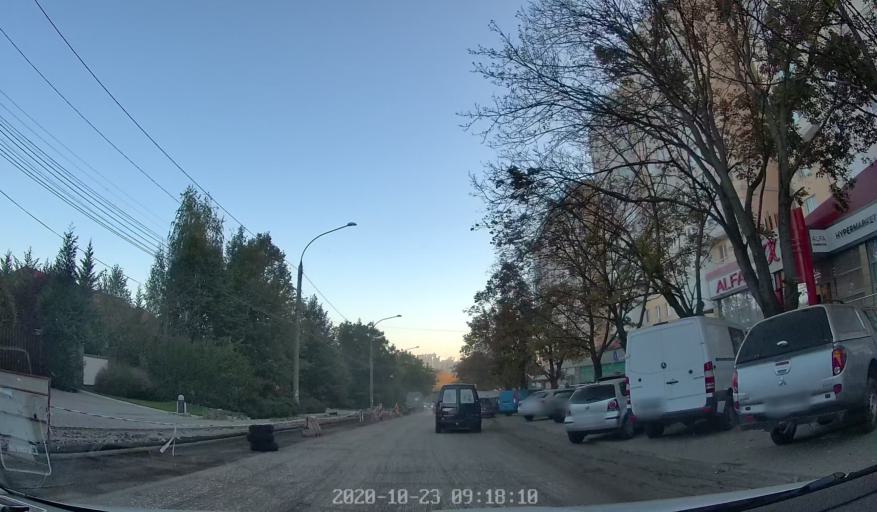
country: MD
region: Chisinau
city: Chisinau
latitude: 46.9969
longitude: 28.8341
